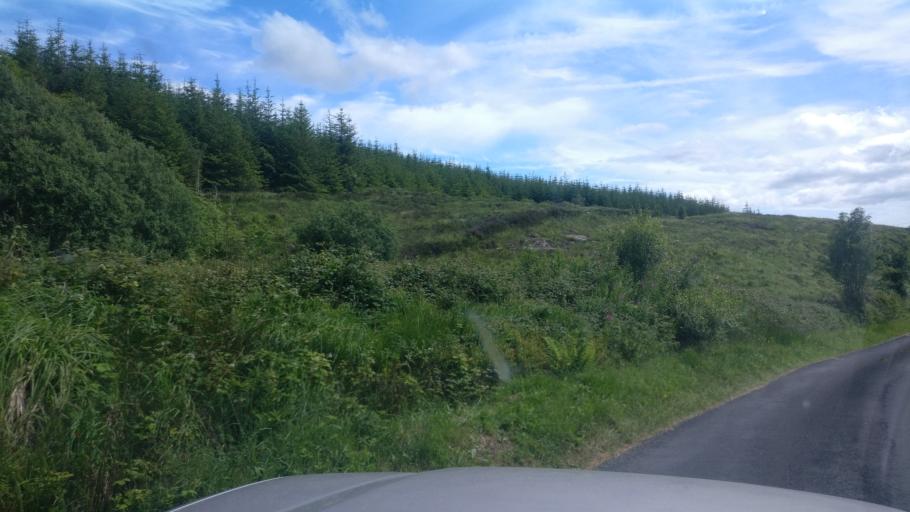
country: IE
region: Connaught
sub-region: County Galway
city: Gort
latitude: 53.0794
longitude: -8.7095
